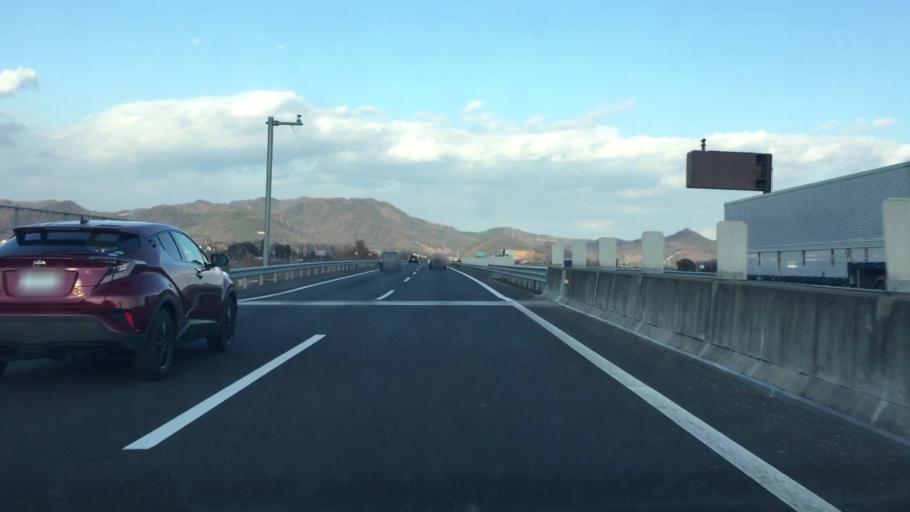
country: JP
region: Gunma
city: Ota
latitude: 36.3329
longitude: 139.3942
